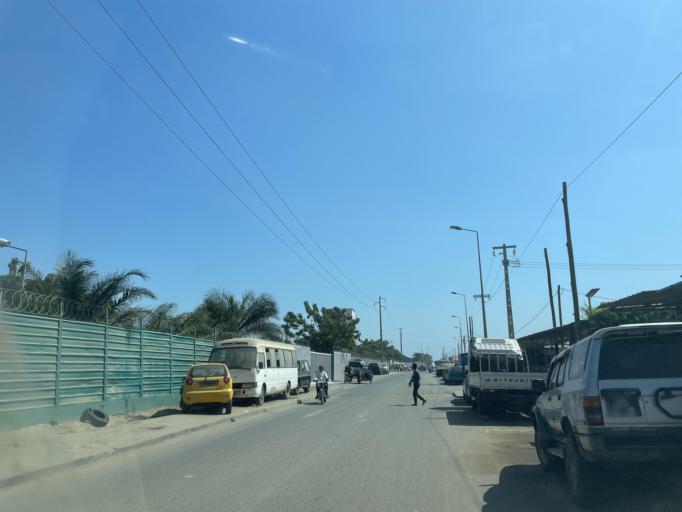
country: AO
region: Luanda
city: Luanda
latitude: -8.7656
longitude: 13.4037
